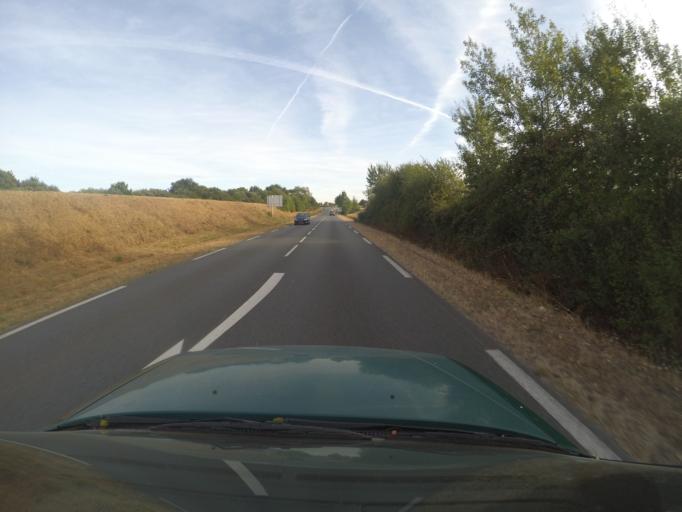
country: FR
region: Pays de la Loire
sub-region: Departement de la Vendee
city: Bouffere
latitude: 46.9729
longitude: -1.3307
